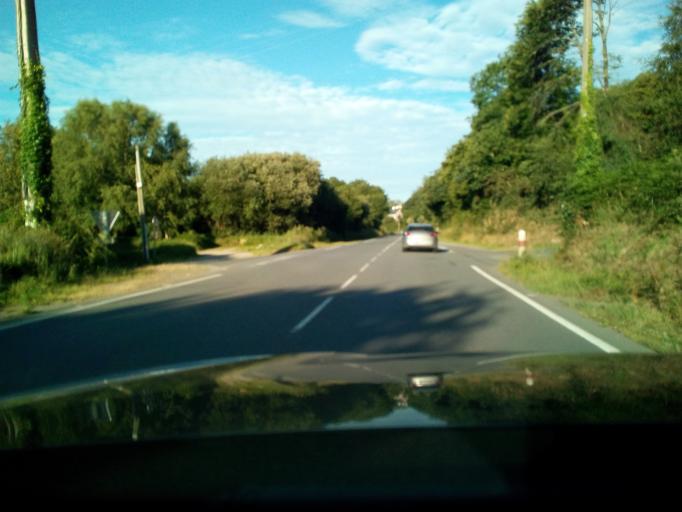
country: FR
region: Brittany
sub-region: Departement du Finistere
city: Landerneau
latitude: 48.4640
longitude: -4.2286
